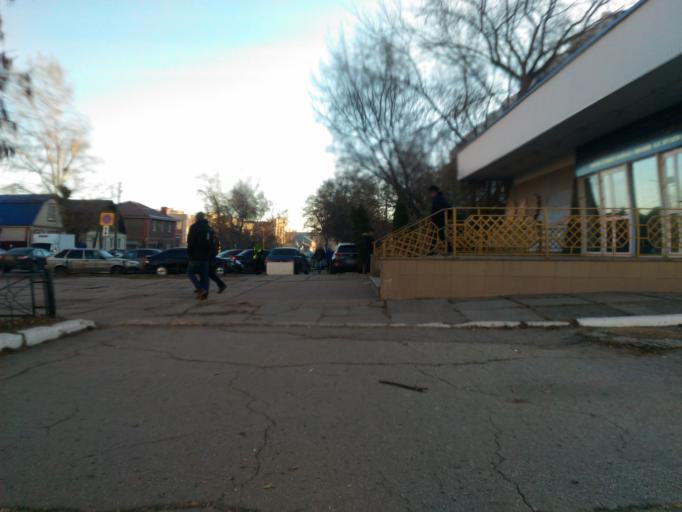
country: RU
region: Ulyanovsk
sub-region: Ulyanovskiy Rayon
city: Ulyanovsk
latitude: 54.3267
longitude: 48.3940
